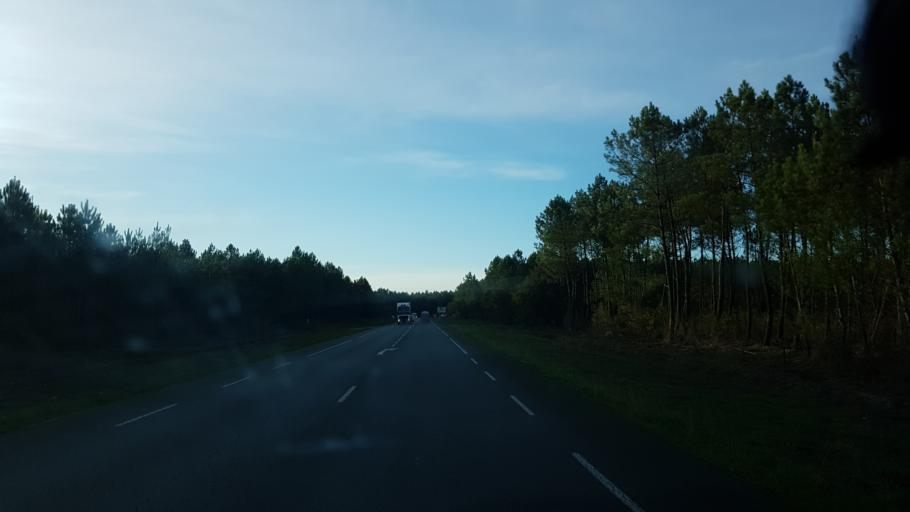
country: FR
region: Aquitaine
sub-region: Departement de la Gironde
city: Martignas-sur-Jalle
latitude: 44.8331
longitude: -0.7980
